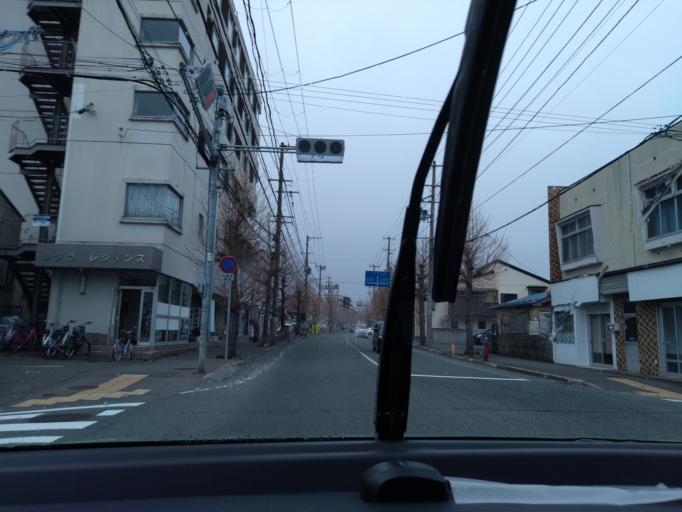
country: JP
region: Iwate
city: Morioka-shi
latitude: 39.7077
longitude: 141.1469
